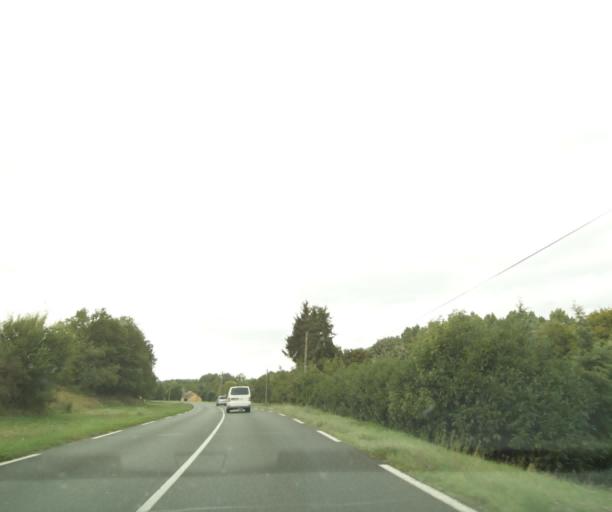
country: FR
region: Centre
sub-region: Departement d'Indre-et-Loire
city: Perrusson
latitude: 47.0689
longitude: 1.0779
